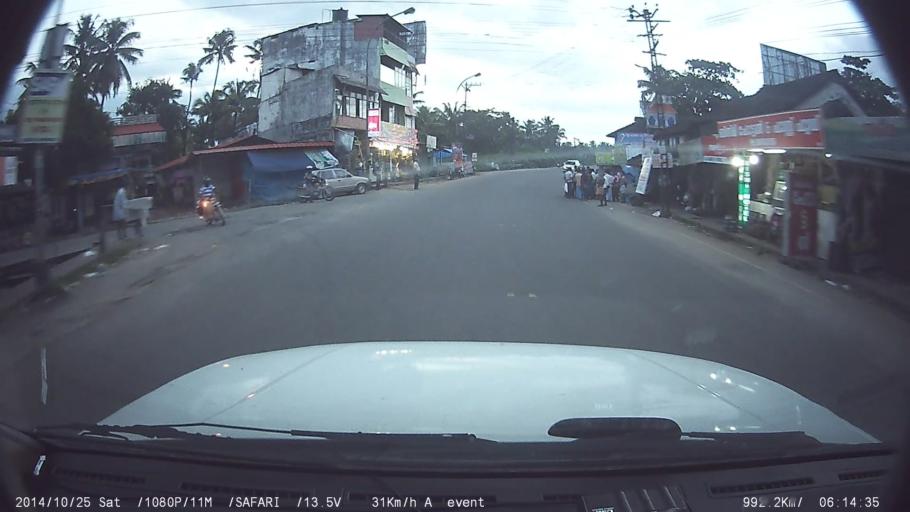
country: IN
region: Kerala
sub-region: Ernakulam
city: Perumpavur
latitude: 10.1360
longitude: 76.4674
